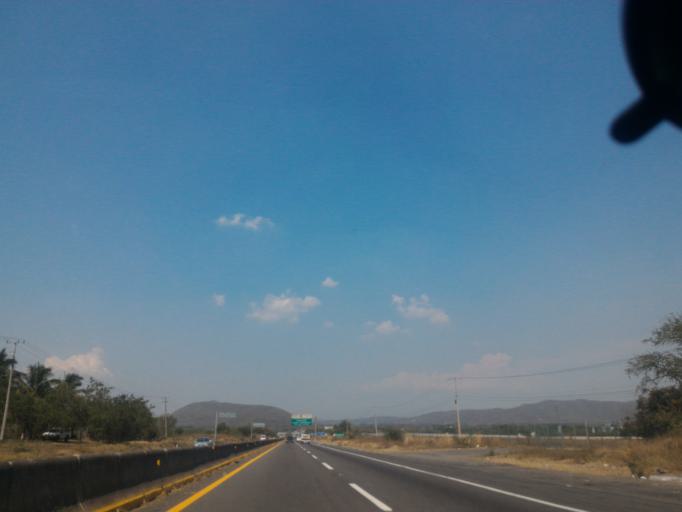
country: MX
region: Colima
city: Madrid
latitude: 19.1070
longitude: -103.7759
